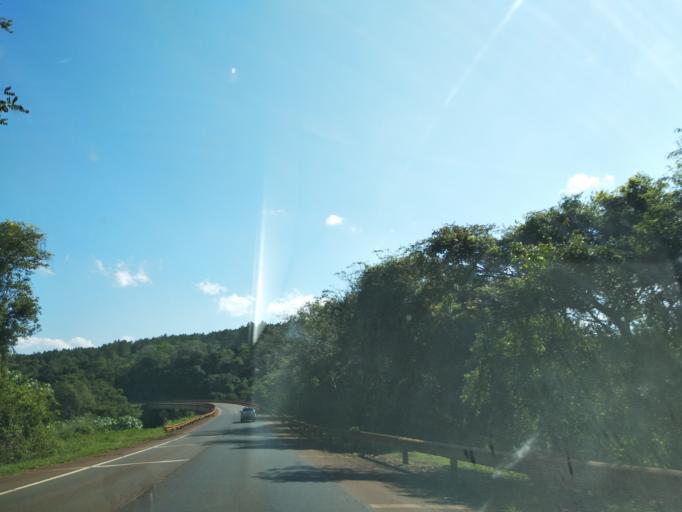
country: AR
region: Misiones
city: Puerto Piray
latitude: -26.4803
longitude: -54.6549
